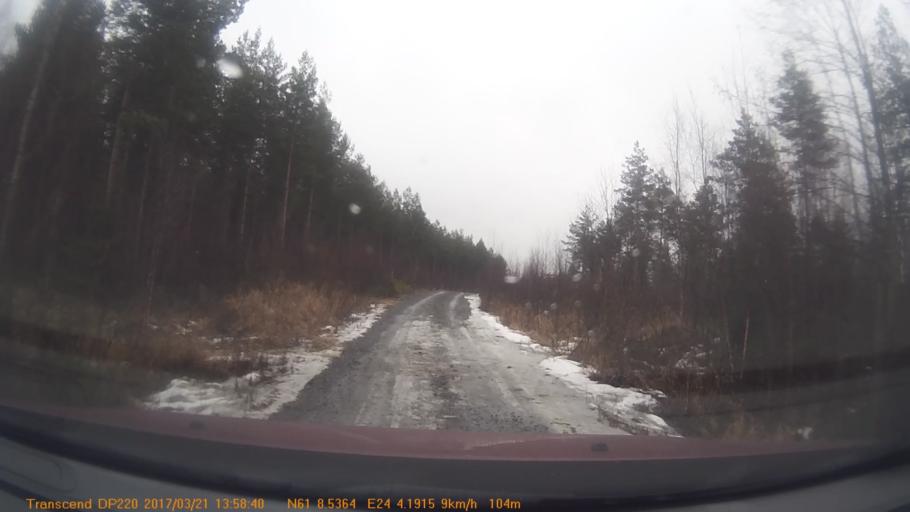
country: FI
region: Haeme
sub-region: Haemeenlinna
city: Kalvola
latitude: 61.1423
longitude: 24.0698
